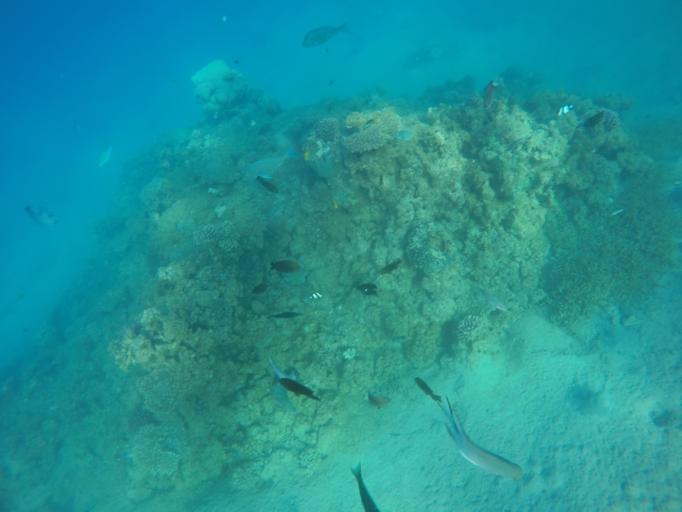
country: EG
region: Red Sea
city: Makadi Bay
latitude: 27.1083
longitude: 33.8329
